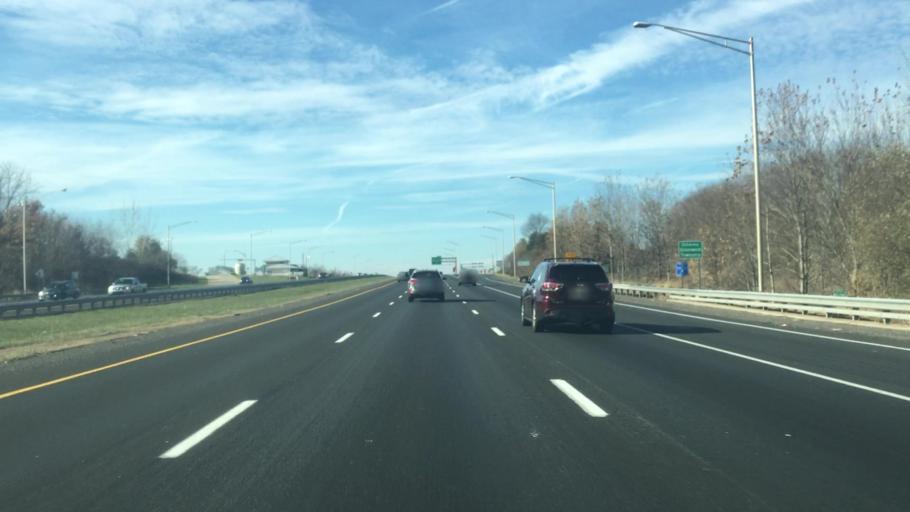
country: US
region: New Jersey
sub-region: Warren County
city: Alpha
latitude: 40.6620
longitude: -75.0797
